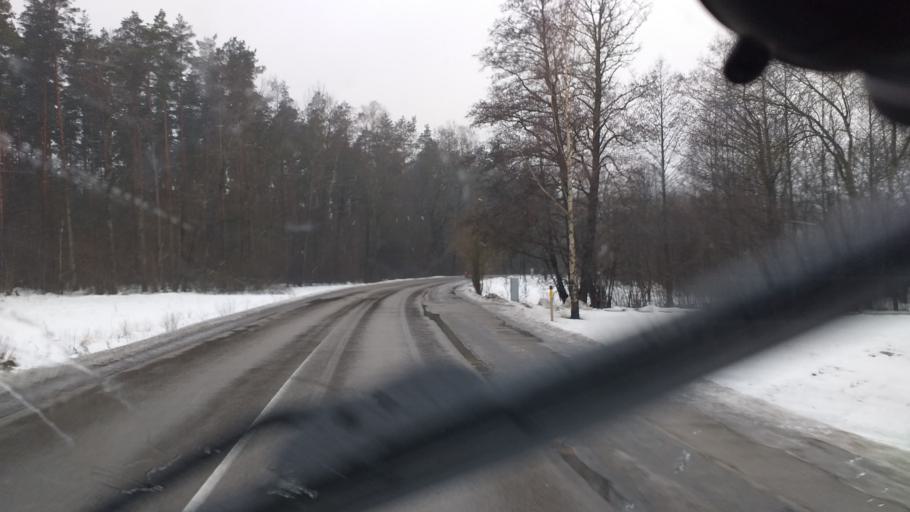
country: LV
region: Riga
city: Daugavgriva
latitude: 56.9833
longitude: 23.9986
